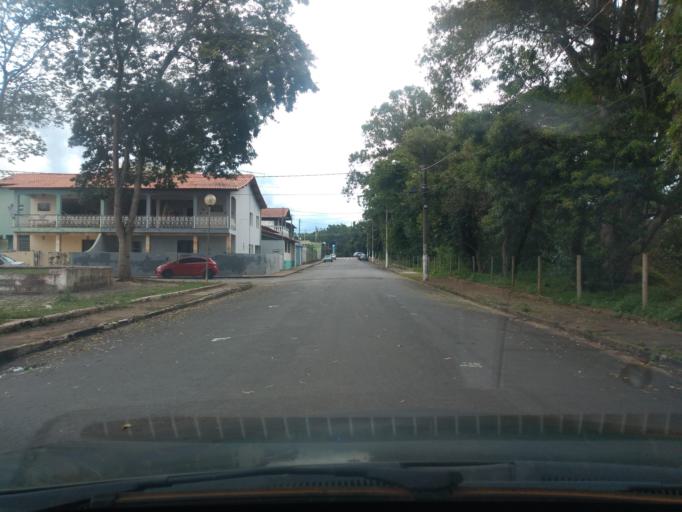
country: BR
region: Minas Gerais
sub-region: Tres Coracoes
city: Tres Coracoes
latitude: -21.7015
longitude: -45.2529
